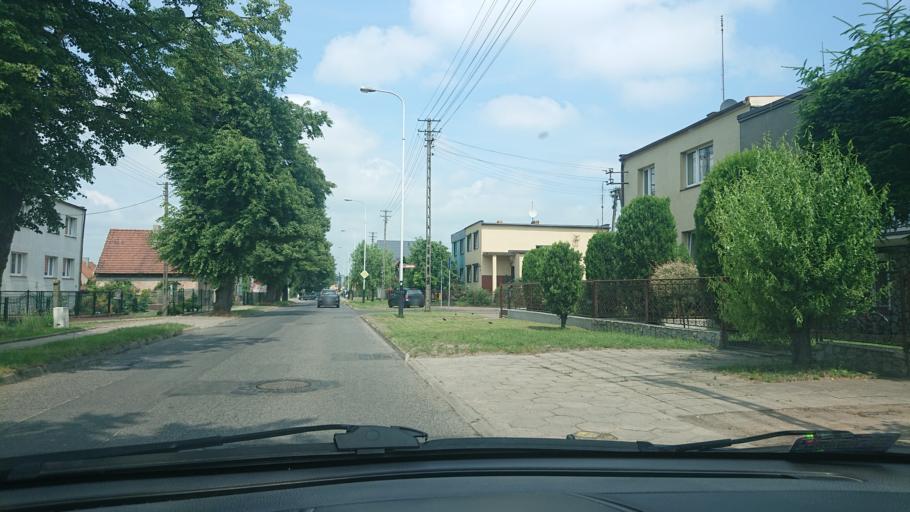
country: PL
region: Greater Poland Voivodeship
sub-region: Powiat gnieznienski
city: Gniezno
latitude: 52.5230
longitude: 17.5816
